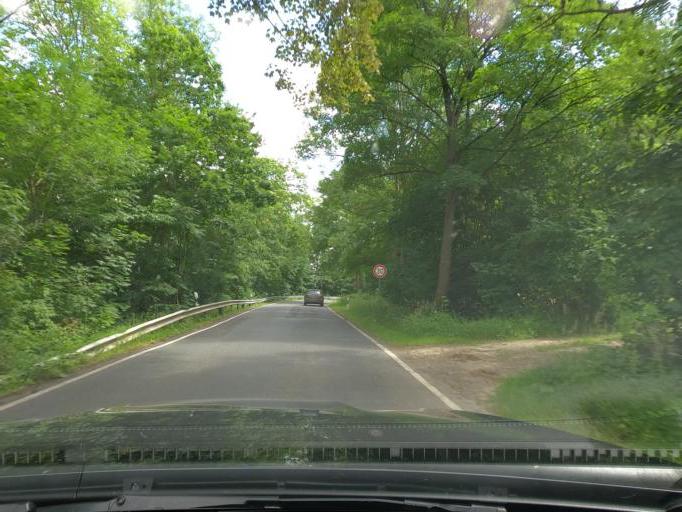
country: DE
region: Lower Saxony
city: Elbe
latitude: 52.1217
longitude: 10.2963
